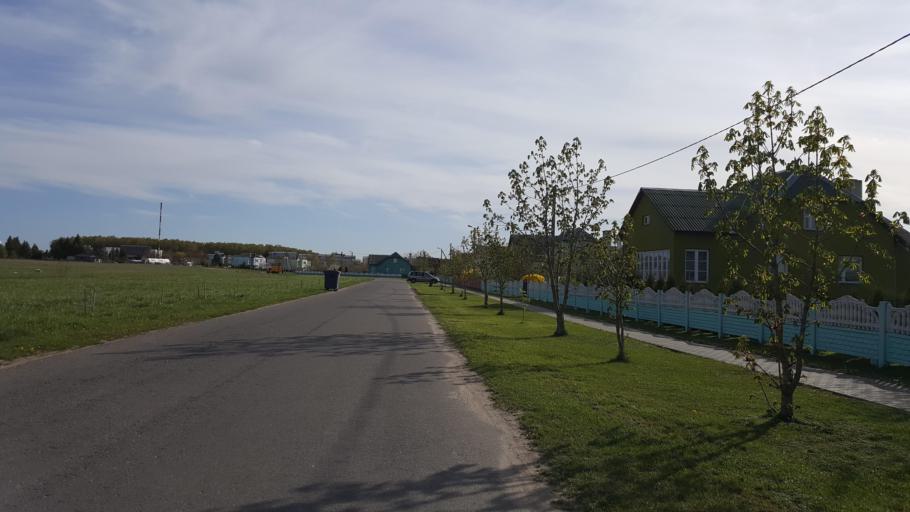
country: BY
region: Brest
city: Vysokaye
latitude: 52.4074
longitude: 23.4647
